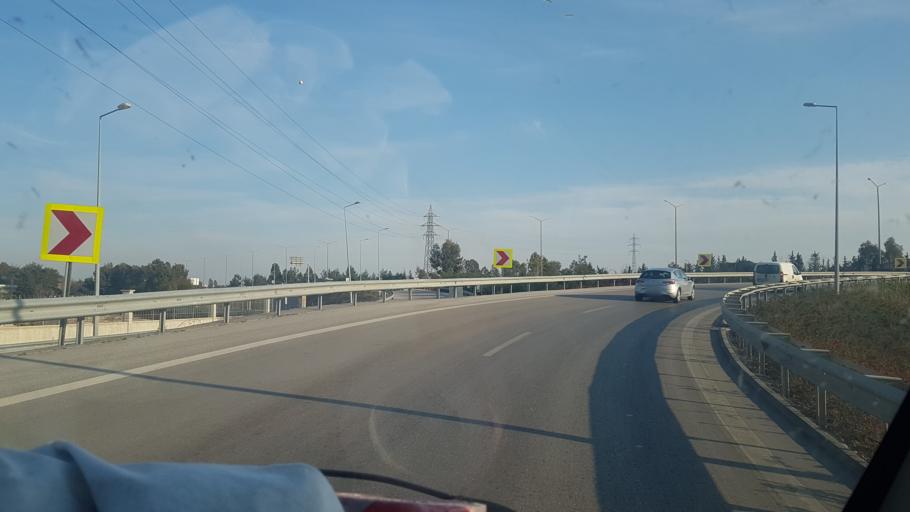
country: TR
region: Adana
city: Adana
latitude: 37.0256
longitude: 35.3451
